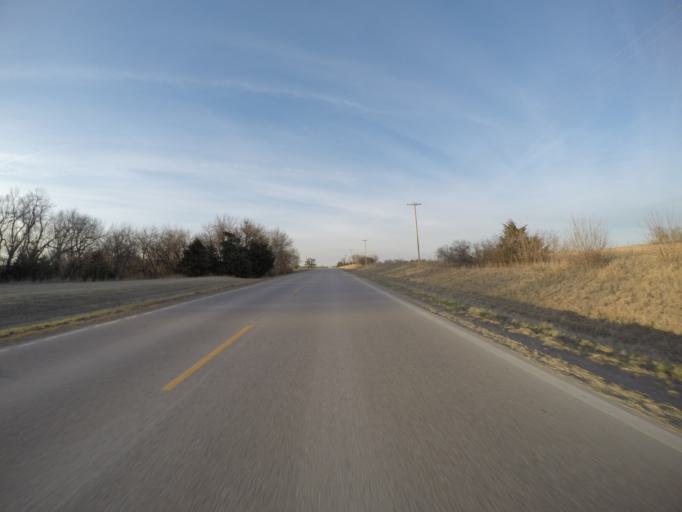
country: US
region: Kansas
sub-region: Riley County
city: Fort Riley North
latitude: 39.3097
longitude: -96.8308
